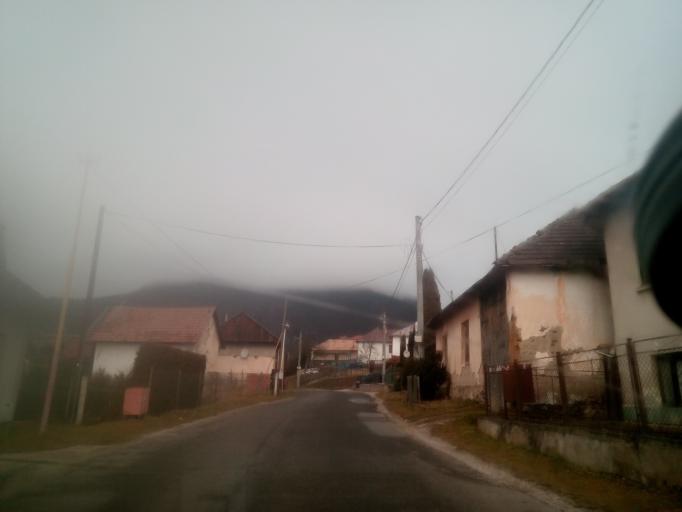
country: SK
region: Kosicky
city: Krompachy
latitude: 48.9326
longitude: 20.9401
